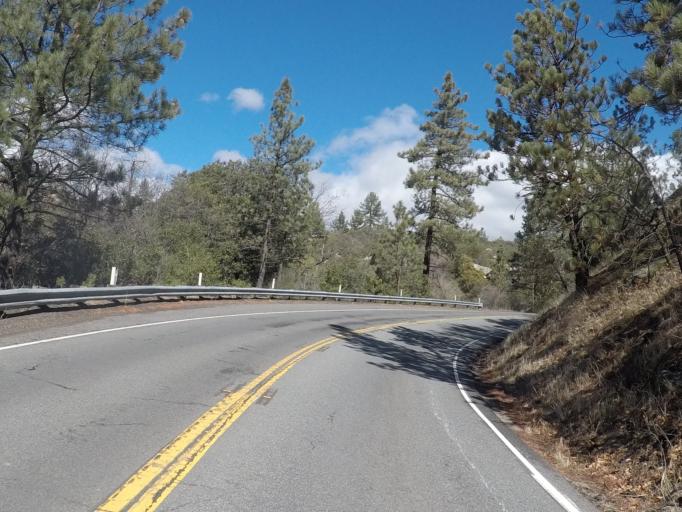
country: US
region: California
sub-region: Riverside County
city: Idyllwild
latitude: 33.7049
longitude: -116.7345
